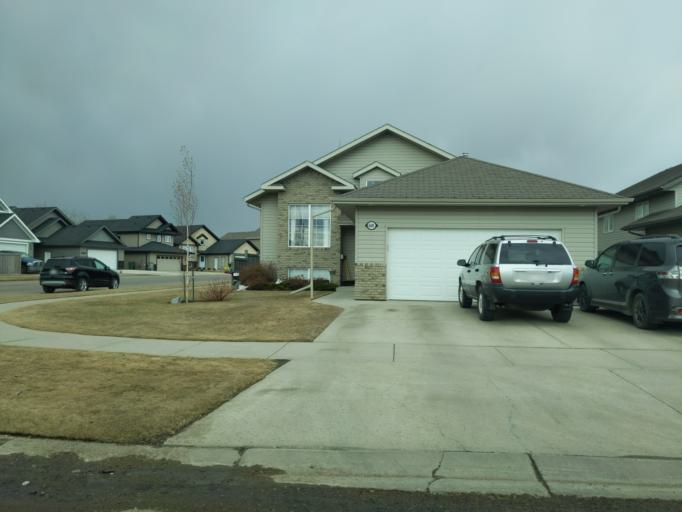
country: CA
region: Saskatchewan
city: Lloydminster
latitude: 53.2555
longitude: -110.0369
